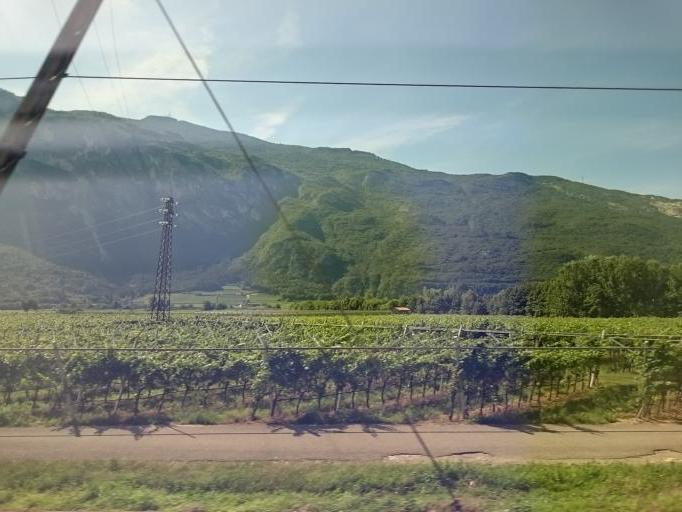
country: IT
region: Trentino-Alto Adige
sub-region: Provincia di Trento
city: Nomi
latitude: 45.9263
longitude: 11.0802
